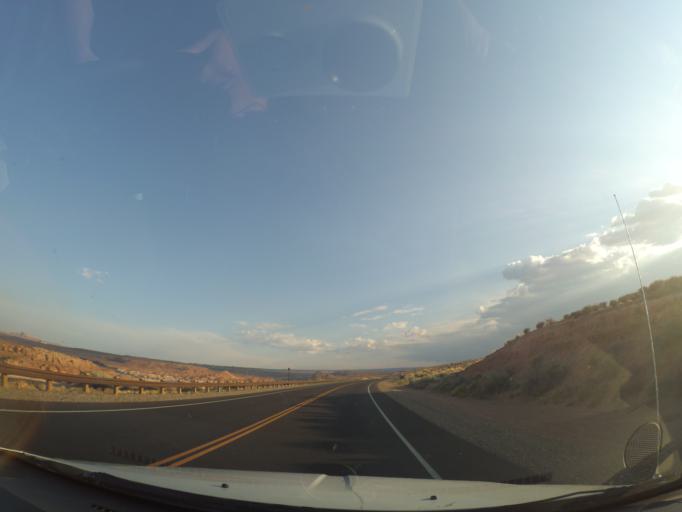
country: US
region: Arizona
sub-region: Coconino County
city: Page
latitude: 36.9677
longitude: -111.4898
